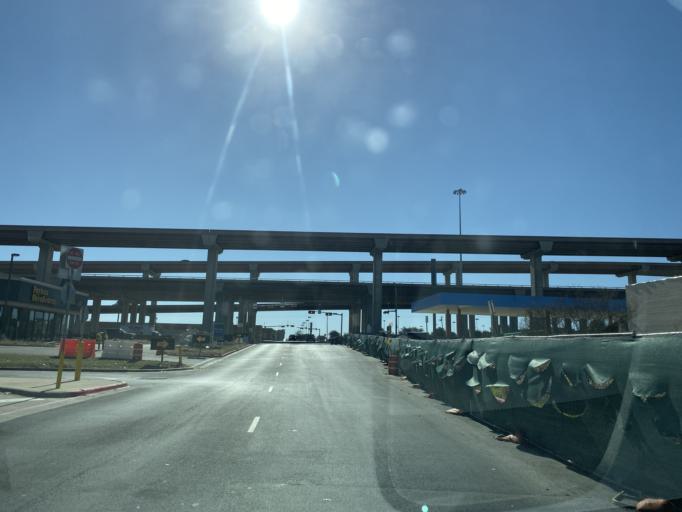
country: US
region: Texas
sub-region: Williamson County
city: Round Rock
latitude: 30.4822
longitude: -97.6703
